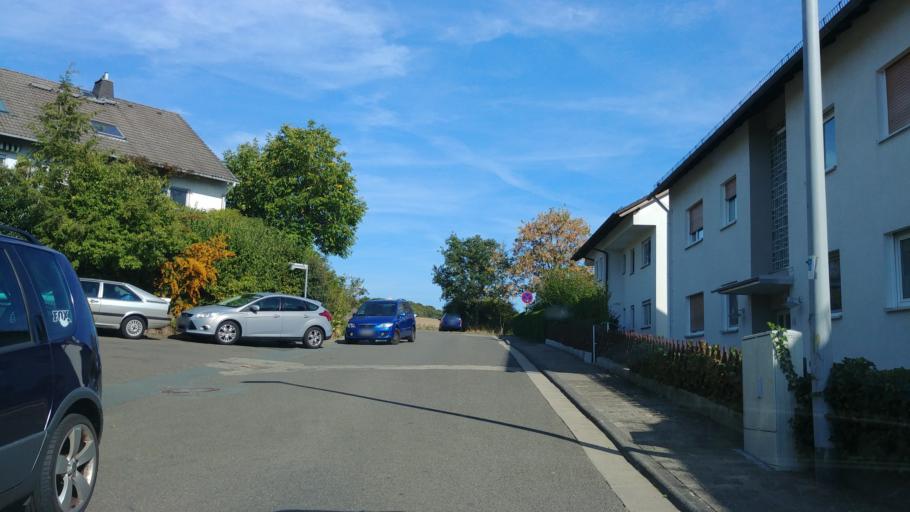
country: DE
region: Hesse
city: Taunusstein
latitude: 50.2075
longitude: 8.1403
